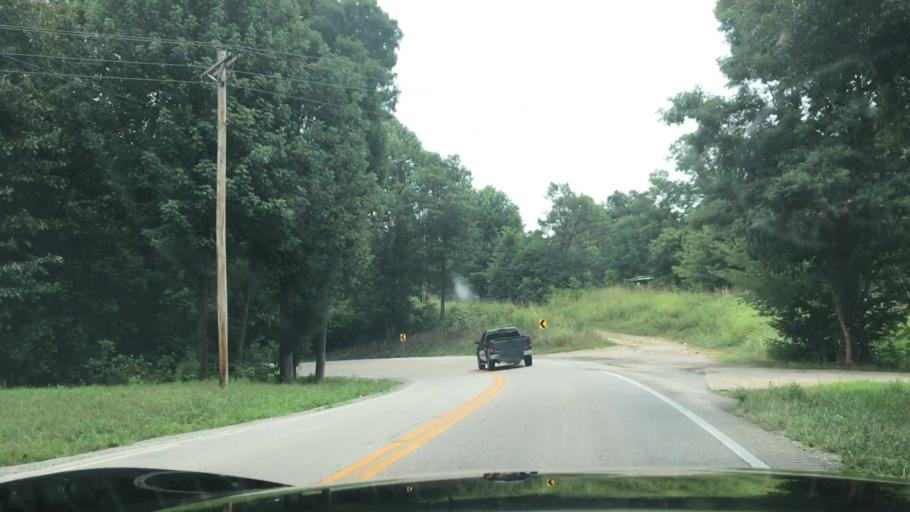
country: US
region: Kentucky
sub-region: Butler County
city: Morgantown
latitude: 37.2076
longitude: -86.7267
